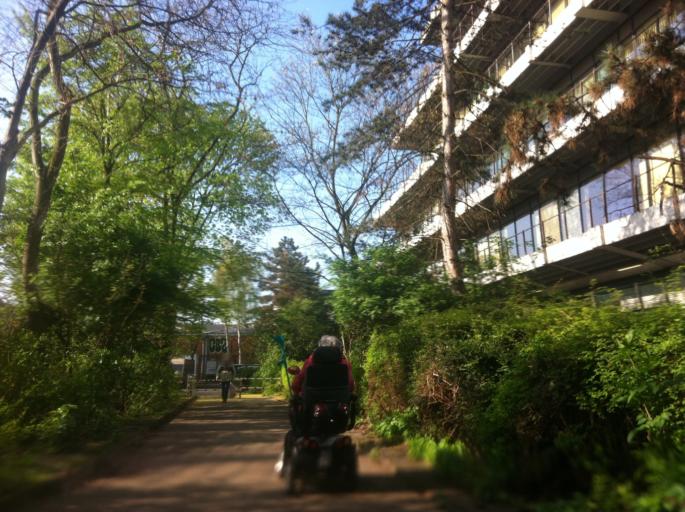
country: DE
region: North Rhine-Westphalia
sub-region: Regierungsbezirk Koln
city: Neuehrenfeld
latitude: 50.9469
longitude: 6.9278
